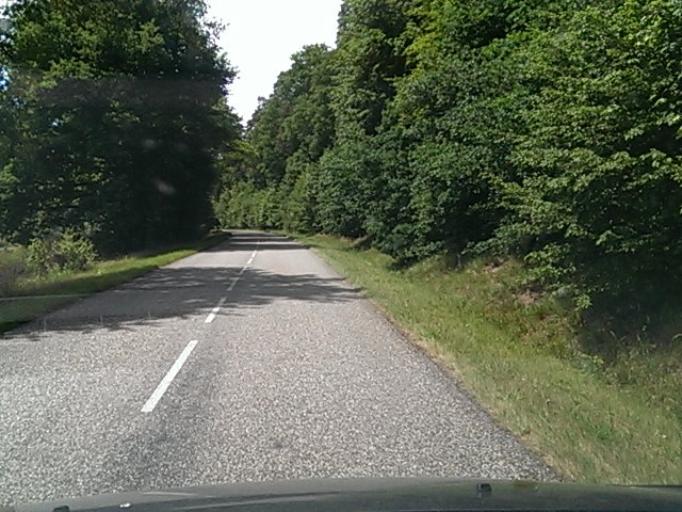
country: DE
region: Rheinland-Pfalz
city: Eppenbrunn
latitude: 49.0512
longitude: 7.5998
